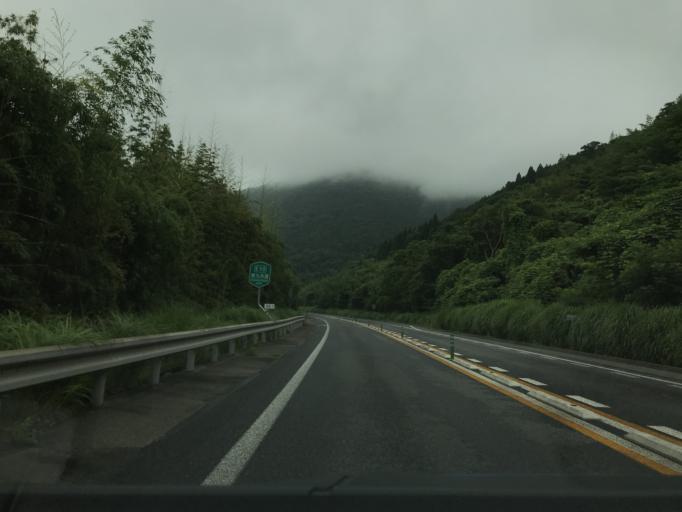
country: JP
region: Oita
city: Bungo-Takada-shi
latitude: 33.4927
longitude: 131.3204
